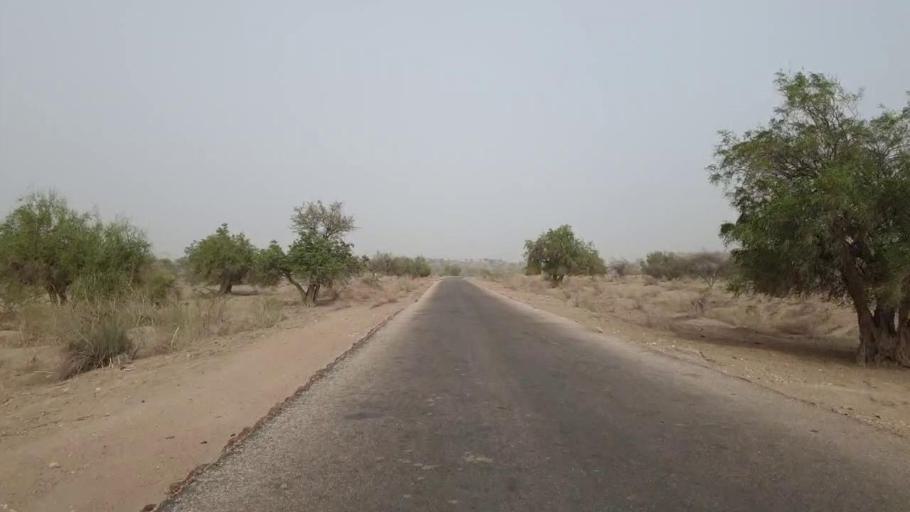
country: PK
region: Sindh
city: Islamkot
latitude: 24.5908
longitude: 70.2865
